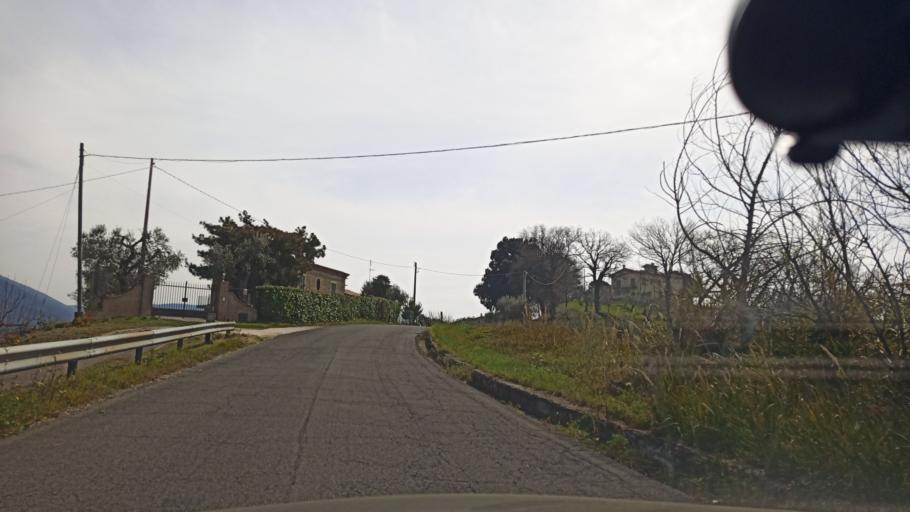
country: IT
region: Latium
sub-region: Provincia di Rieti
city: Torri in Sabina
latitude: 42.3462
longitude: 12.6503
